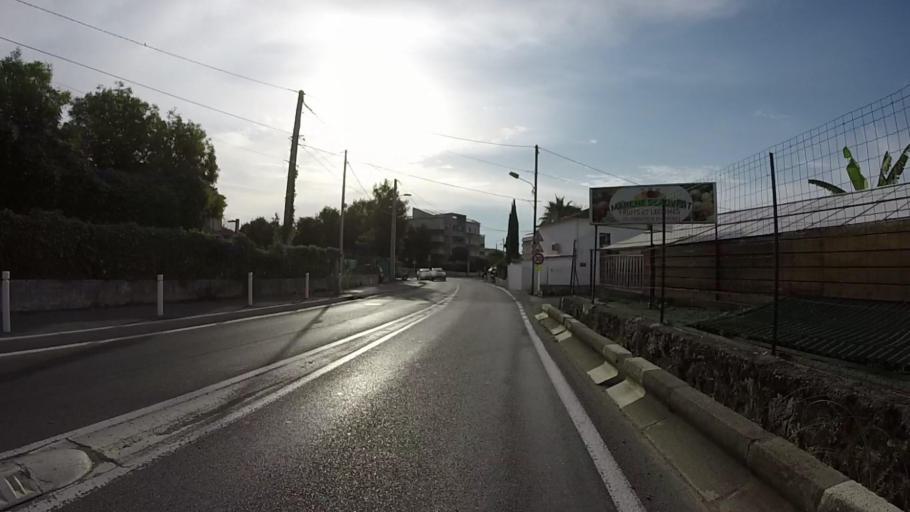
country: FR
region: Provence-Alpes-Cote d'Azur
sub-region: Departement des Alpes-Maritimes
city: Biot
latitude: 43.5961
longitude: 7.1121
